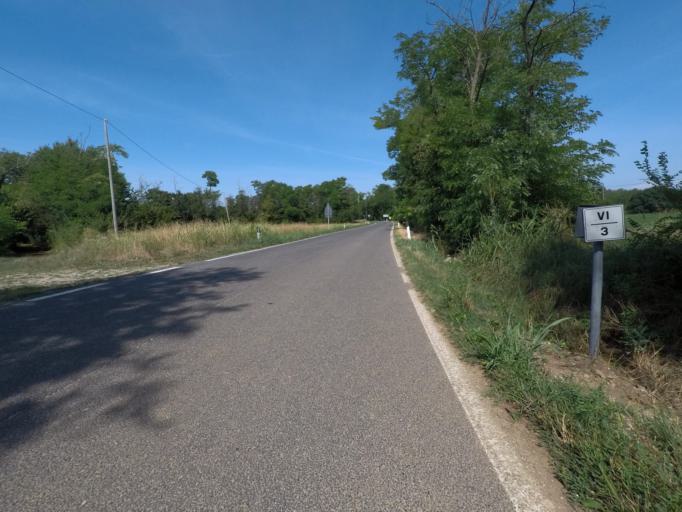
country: IT
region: Friuli Venezia Giulia
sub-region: Provincia di Udine
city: Mereto di Tomba
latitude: 46.0700
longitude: 13.0281
